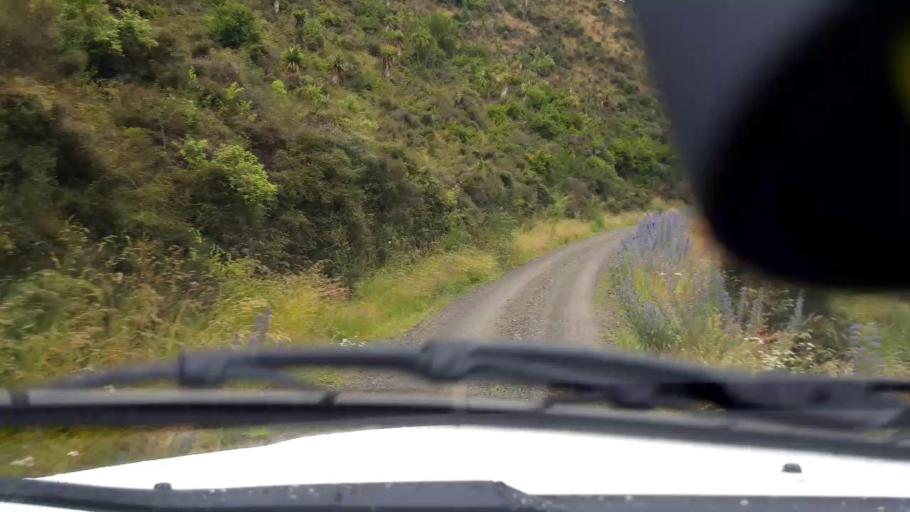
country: NZ
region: Canterbury
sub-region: Timaru District
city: Pleasant Point
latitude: -44.0371
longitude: 171.0098
